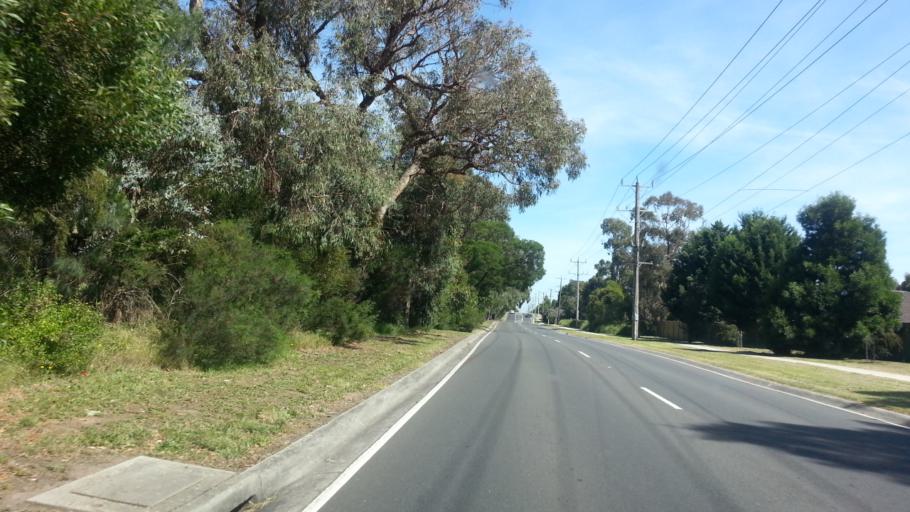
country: AU
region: Victoria
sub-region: Knox
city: Rowville
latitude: -37.9386
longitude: 145.2415
